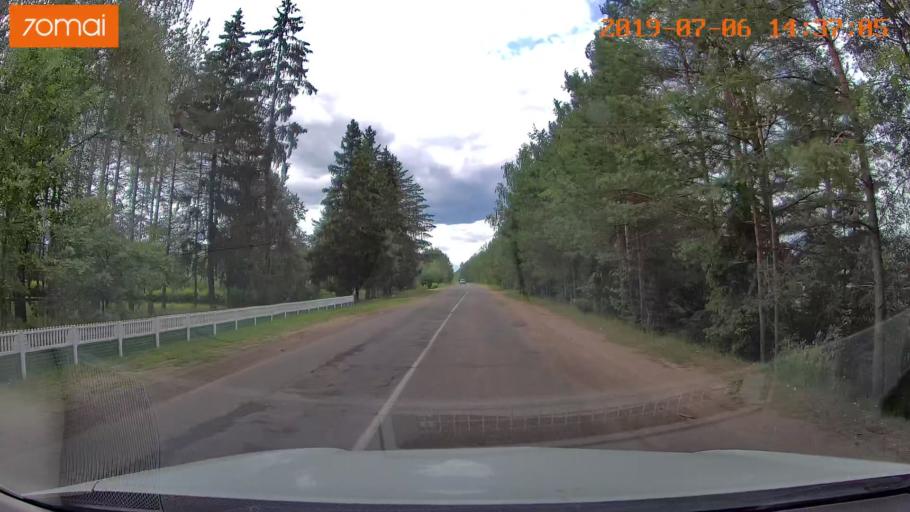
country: BY
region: Minsk
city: Ivyanyets
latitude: 53.8944
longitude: 26.7247
